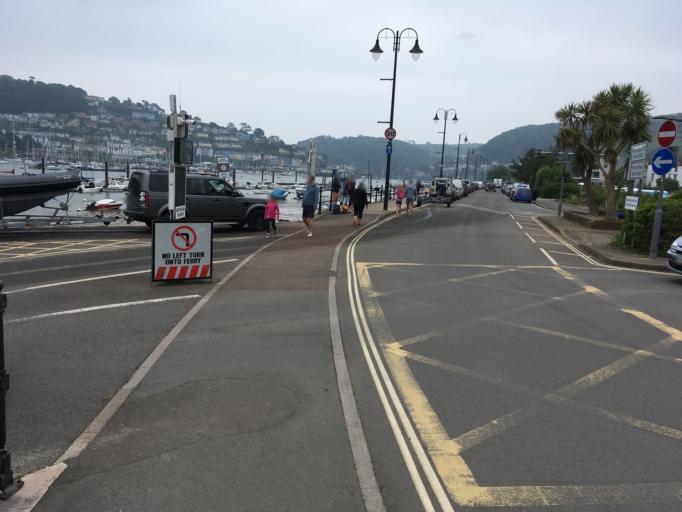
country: GB
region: England
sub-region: Devon
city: Dartmouth
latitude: 50.3566
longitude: -3.5769
